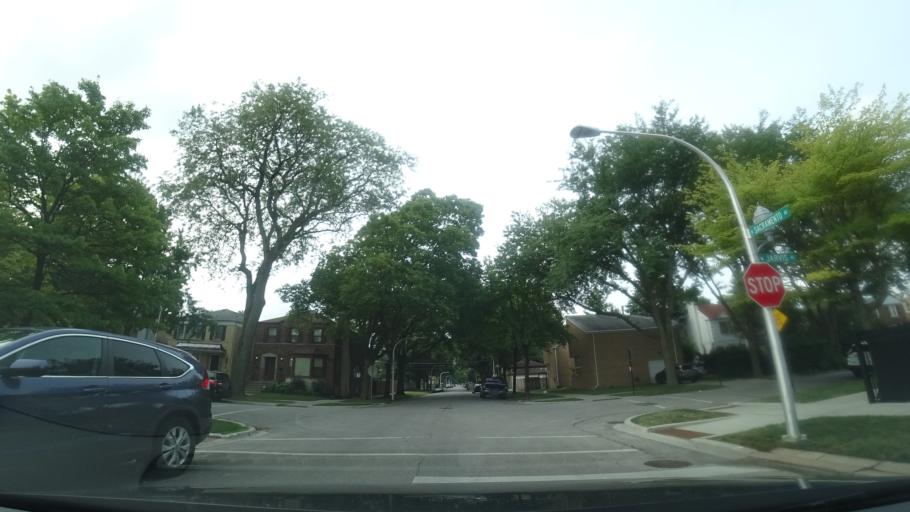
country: US
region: Illinois
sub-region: Cook County
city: Lincolnwood
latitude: 42.0159
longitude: -87.7044
